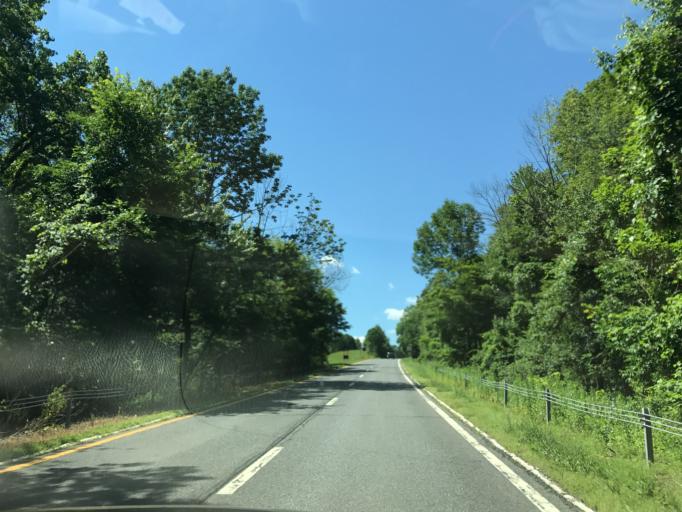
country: US
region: New York
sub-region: Dutchess County
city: Pine Plains
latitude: 41.9362
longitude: -73.7547
